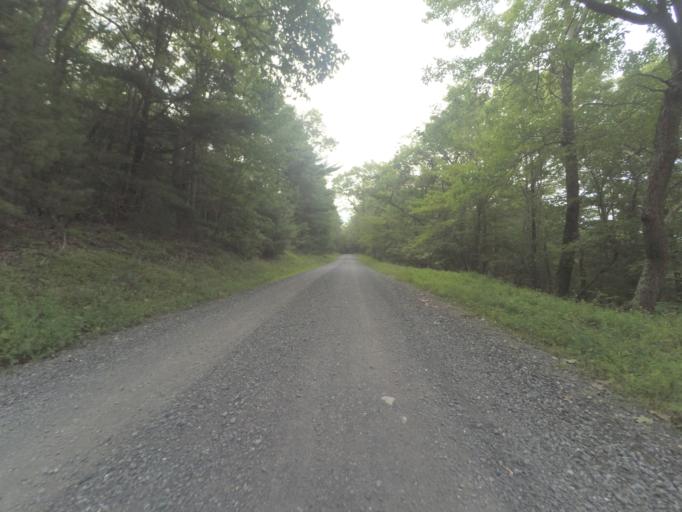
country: US
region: Pennsylvania
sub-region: Centre County
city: Boalsburg
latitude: 40.7192
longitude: -77.7595
